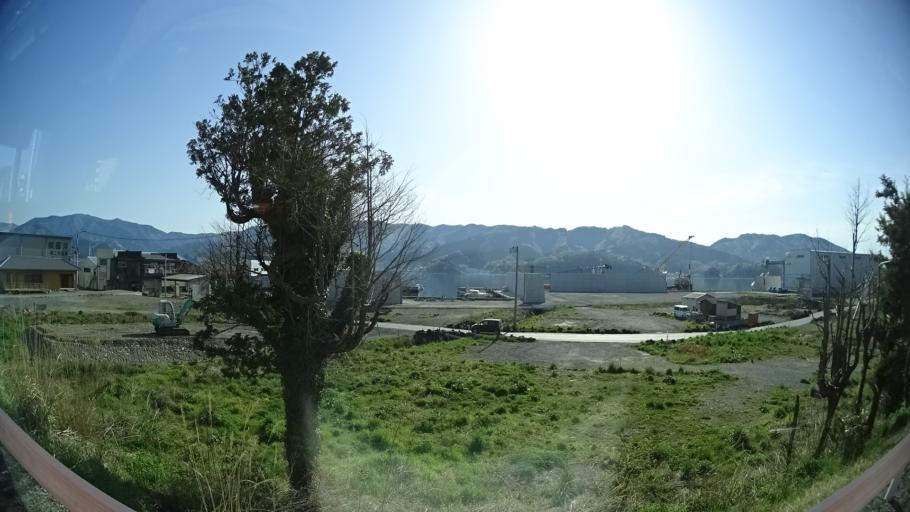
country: JP
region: Iwate
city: Ofunato
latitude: 39.0451
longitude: 141.7225
